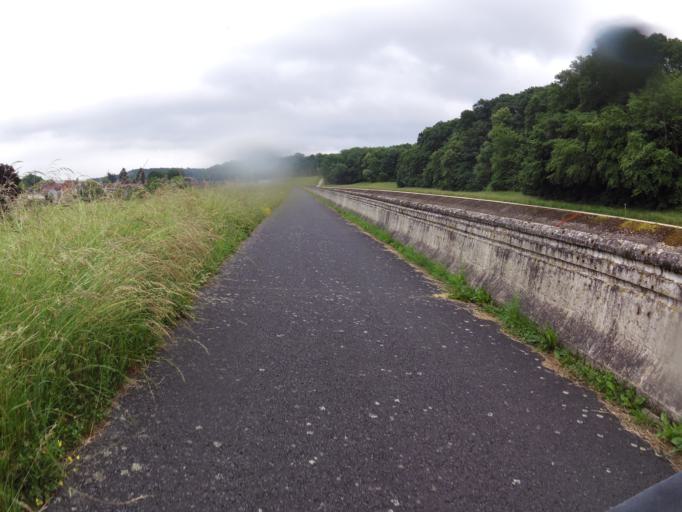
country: FR
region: Champagne-Ardenne
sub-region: Departement de la Haute-Marne
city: Saint-Dizier
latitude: 48.6154
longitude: 4.9011
